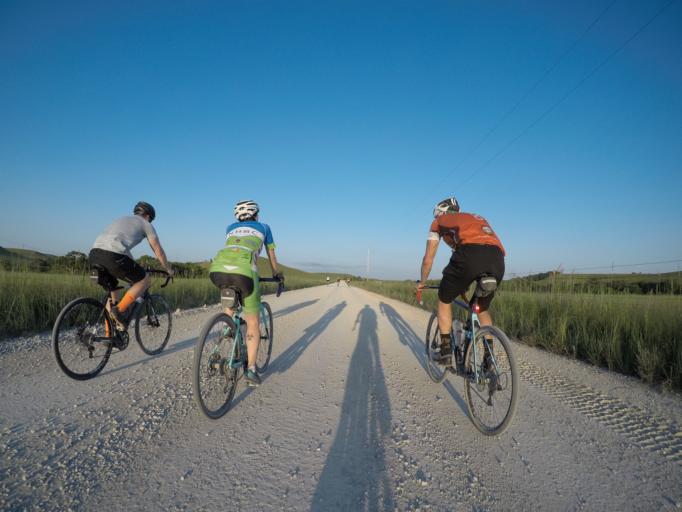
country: US
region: Kansas
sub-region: Riley County
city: Ogden
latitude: 39.0151
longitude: -96.6758
